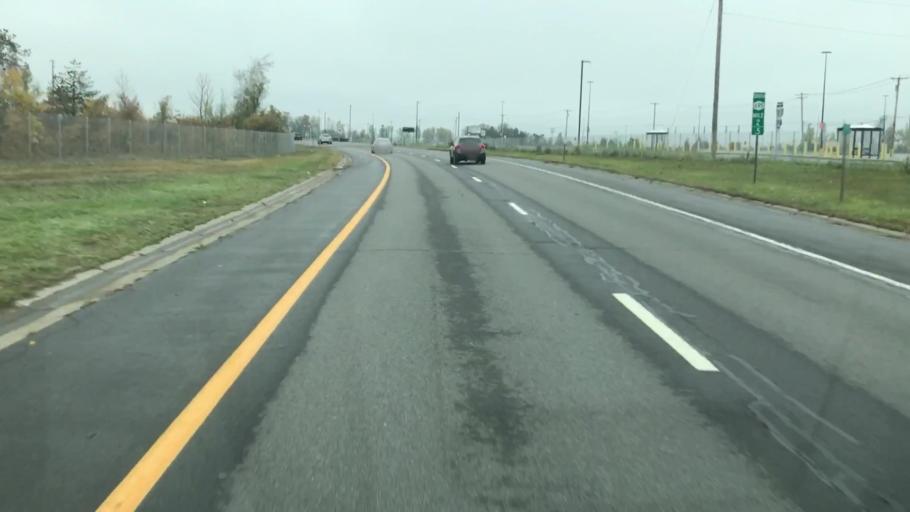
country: US
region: New York
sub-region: Onondaga County
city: Solvay
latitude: 43.0786
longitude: -76.2154
